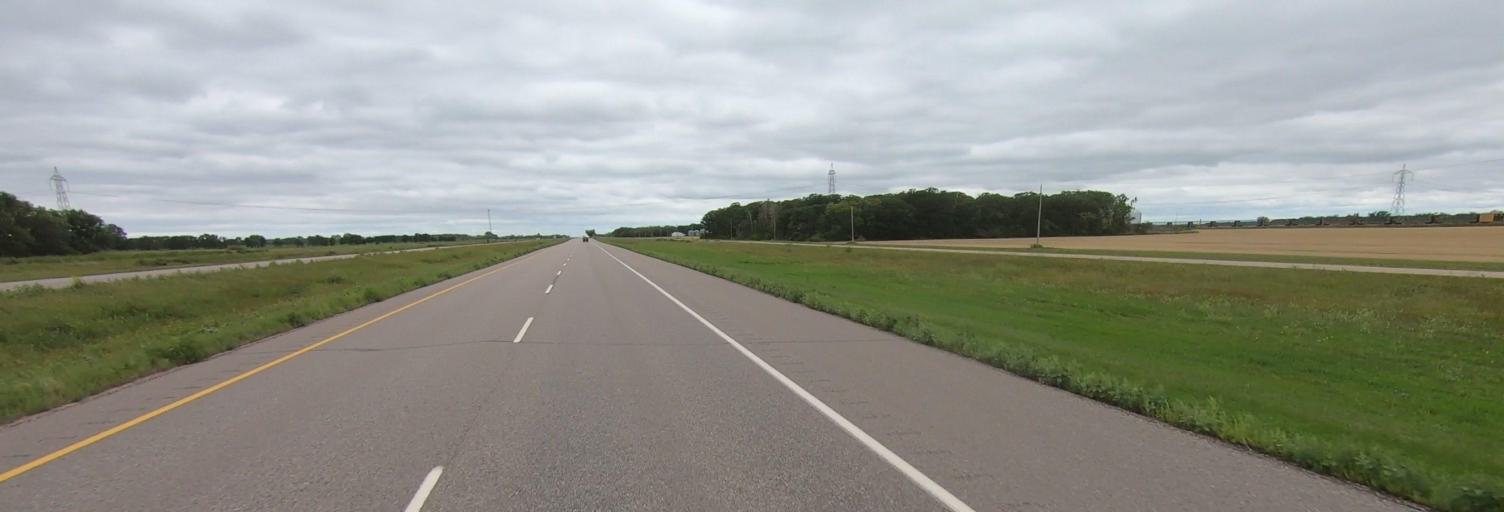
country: CA
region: Manitoba
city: Portage la Prairie
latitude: 49.9751
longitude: -98.5412
